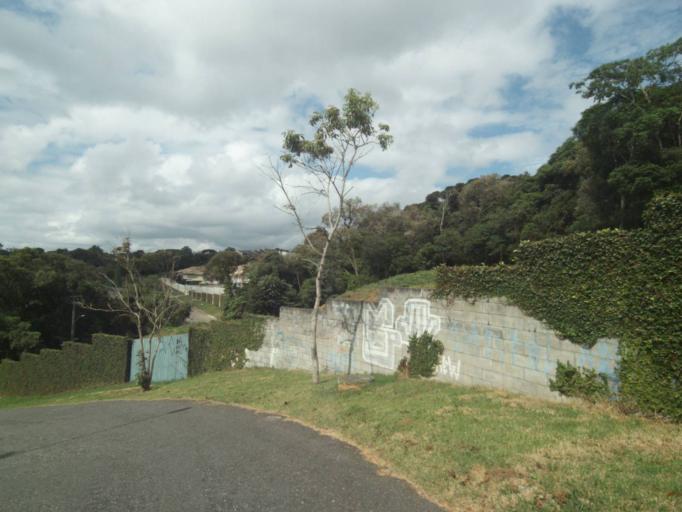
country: BR
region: Parana
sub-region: Curitiba
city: Curitiba
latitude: -25.3820
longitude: -49.2842
